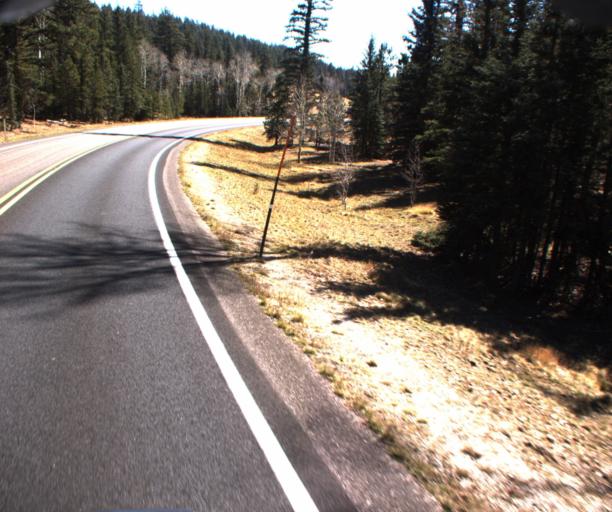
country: US
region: Arizona
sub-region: Coconino County
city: Grand Canyon
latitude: 36.5347
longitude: -112.1534
